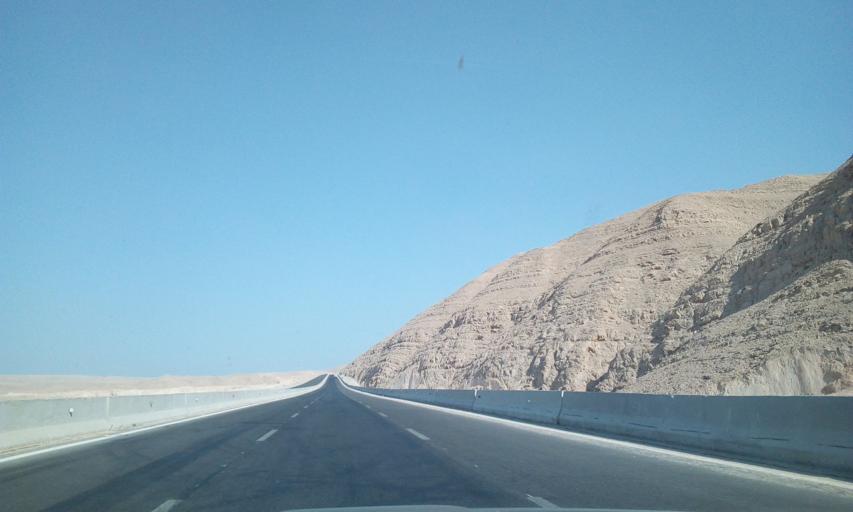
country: EG
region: As Suways
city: Ain Sukhna
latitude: 29.5506
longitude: 32.2870
